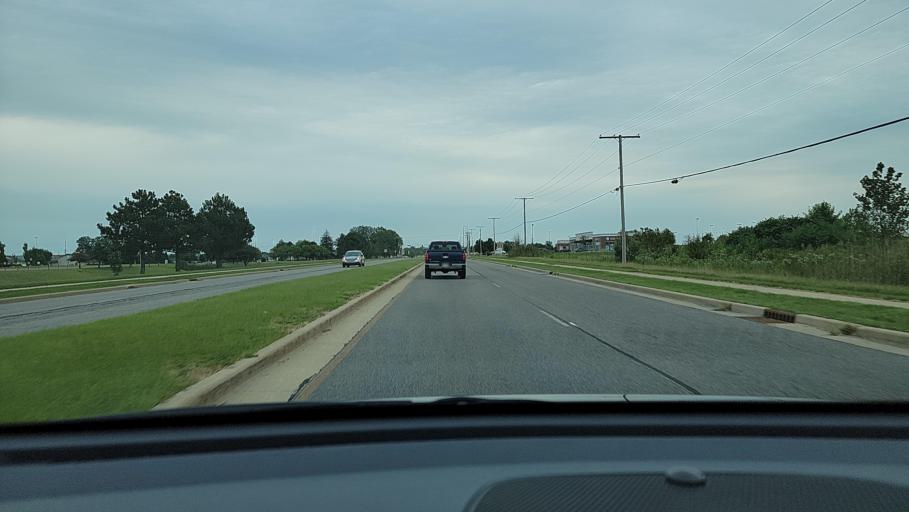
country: US
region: Indiana
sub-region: Porter County
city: Portage
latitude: 41.5505
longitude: -87.1678
